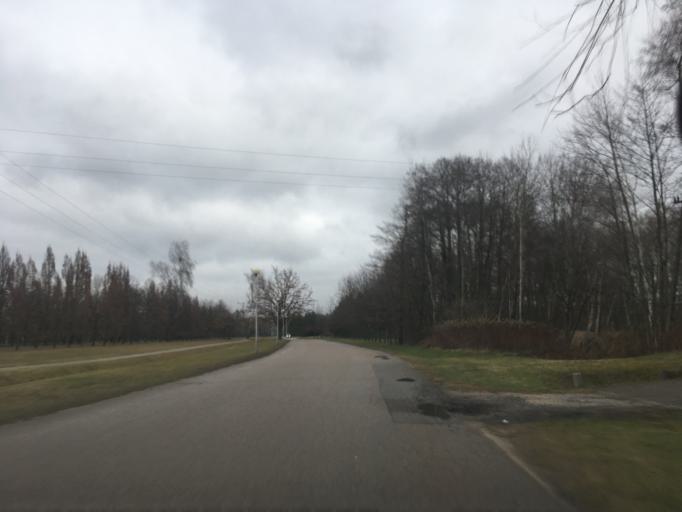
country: PL
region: Masovian Voivodeship
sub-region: Powiat piaseczynski
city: Lesznowola
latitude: 52.0576
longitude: 20.9055
